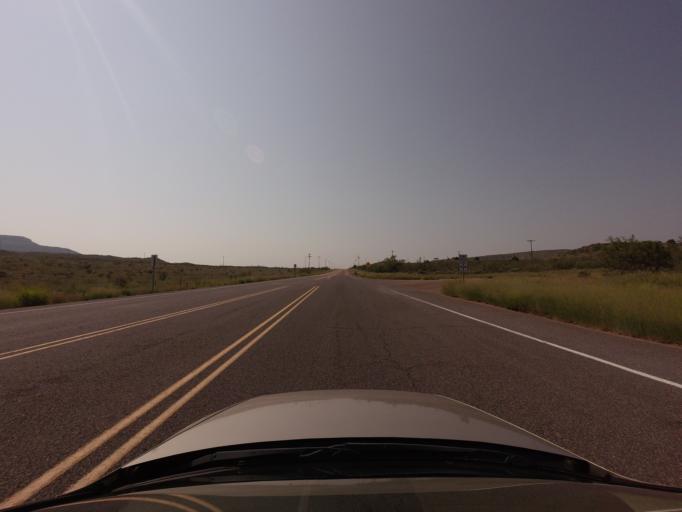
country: US
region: New Mexico
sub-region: Quay County
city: Tucumcari
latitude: 35.1486
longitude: -103.7251
